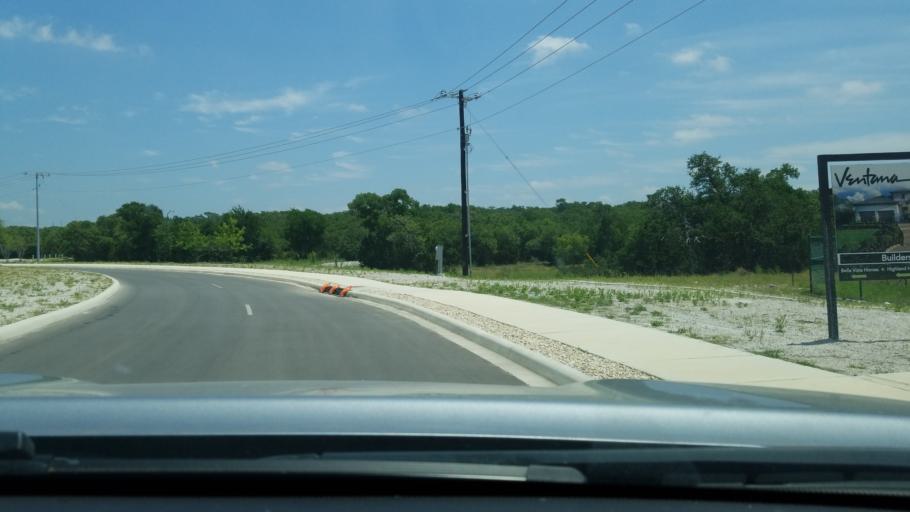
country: US
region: Texas
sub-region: Comal County
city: Bulverde
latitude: 29.7968
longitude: -98.5240
